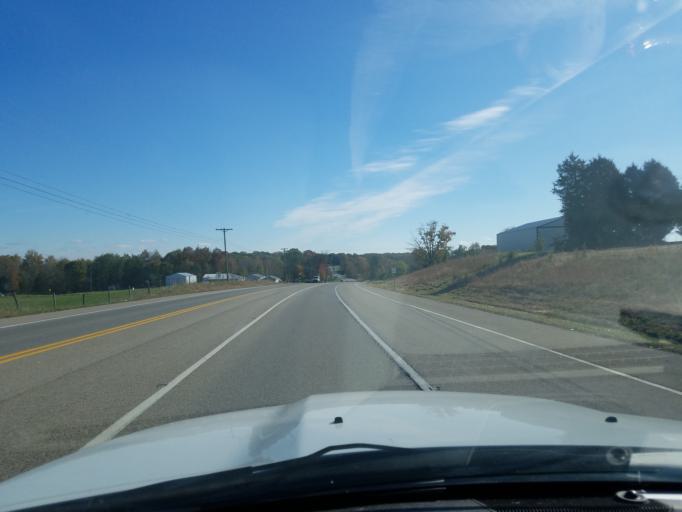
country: US
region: Indiana
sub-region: Jennings County
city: Country Squire Lakes
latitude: 38.9763
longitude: -85.7427
